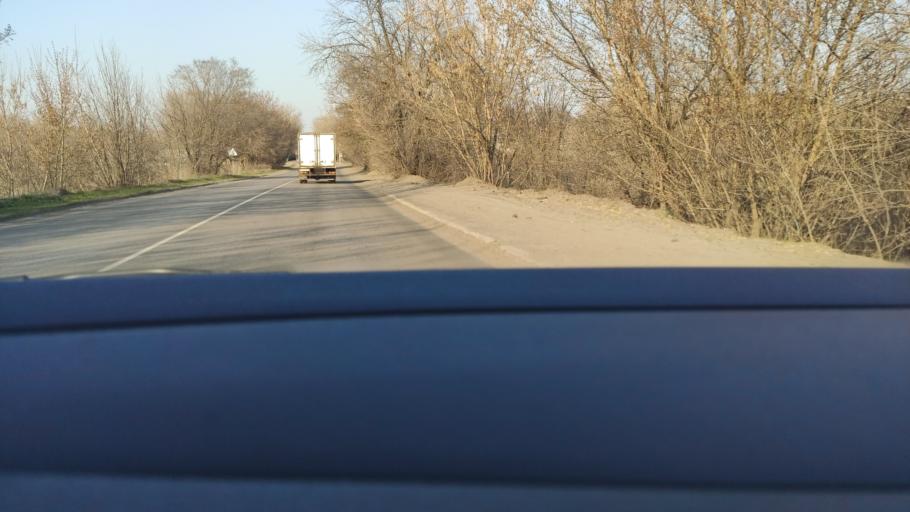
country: RU
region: Voronezj
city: Maslovka
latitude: 51.5782
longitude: 39.3132
